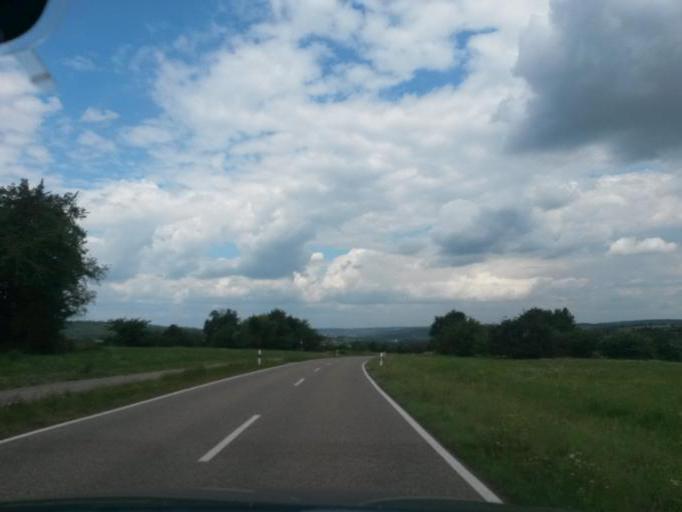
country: DE
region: Baden-Wuerttemberg
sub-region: Karlsruhe Region
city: Neuenburg
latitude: 48.8668
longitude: 8.5357
